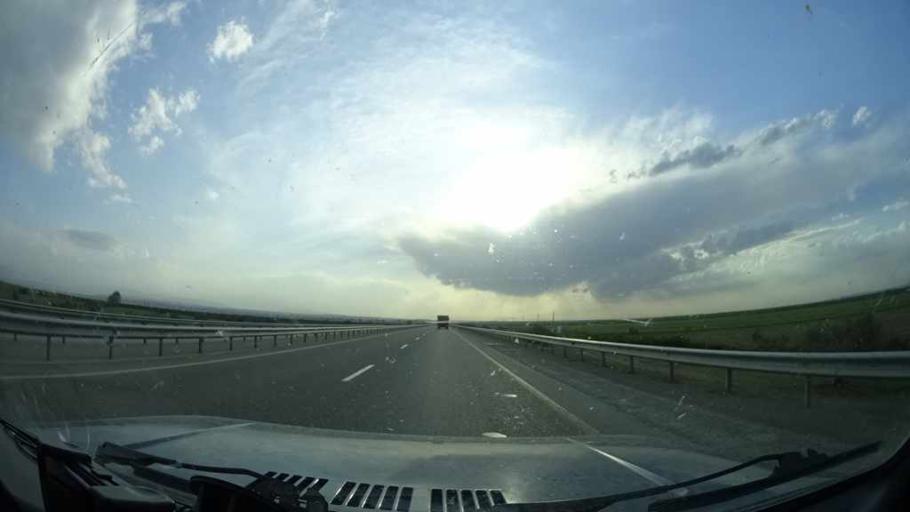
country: AZ
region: Goranboy
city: Goranboy
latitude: 40.6457
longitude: 46.7412
